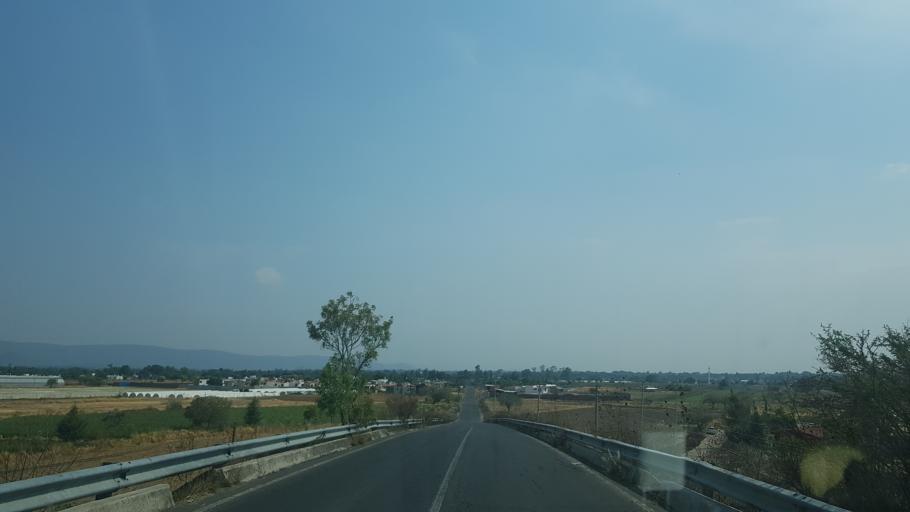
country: MX
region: Puebla
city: San Juan Tianguismanalco
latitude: 18.9340
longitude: -98.4542
